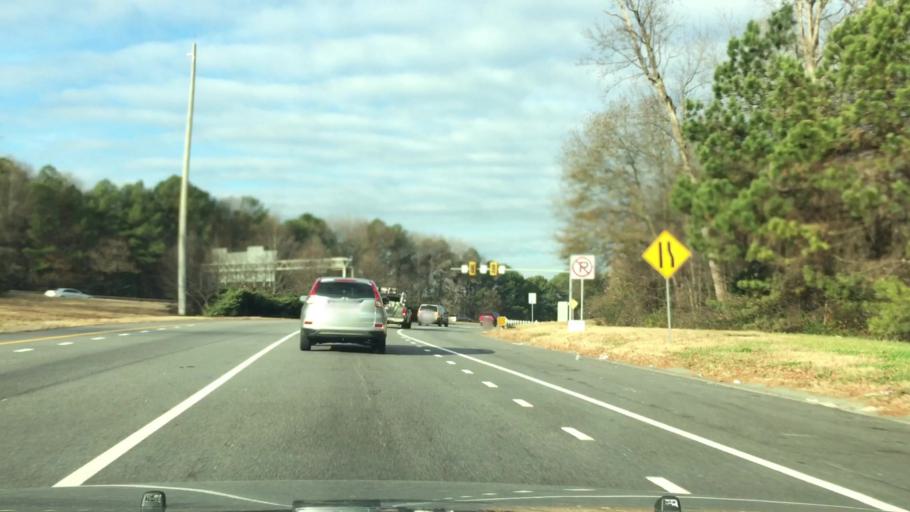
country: US
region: Georgia
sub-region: DeKalb County
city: Doraville
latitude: 33.9158
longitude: -84.2875
